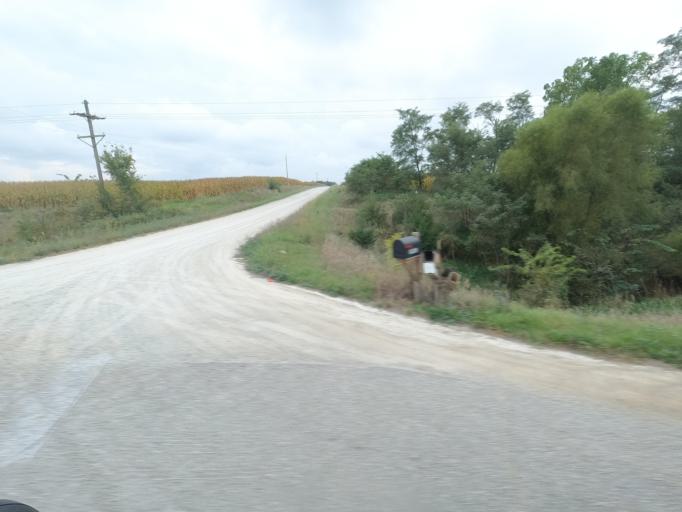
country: US
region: Iowa
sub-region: Van Buren County
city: Keosauqua
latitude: 40.8136
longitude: -91.8913
